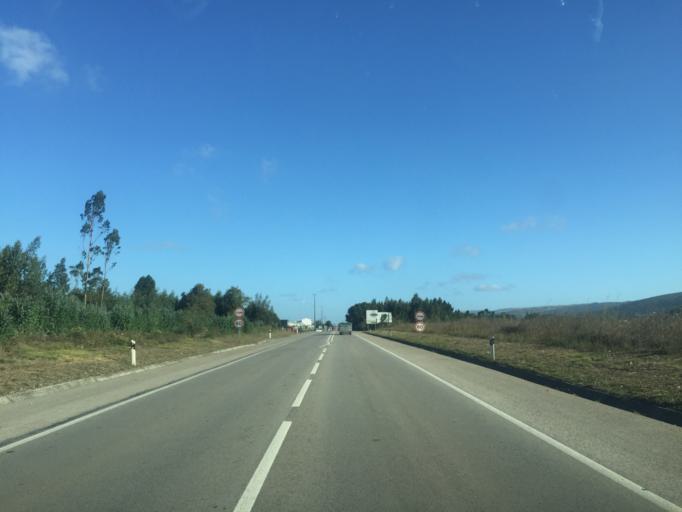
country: PT
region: Leiria
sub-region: Alcobaca
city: Benedita
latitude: 39.4216
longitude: -8.9620
